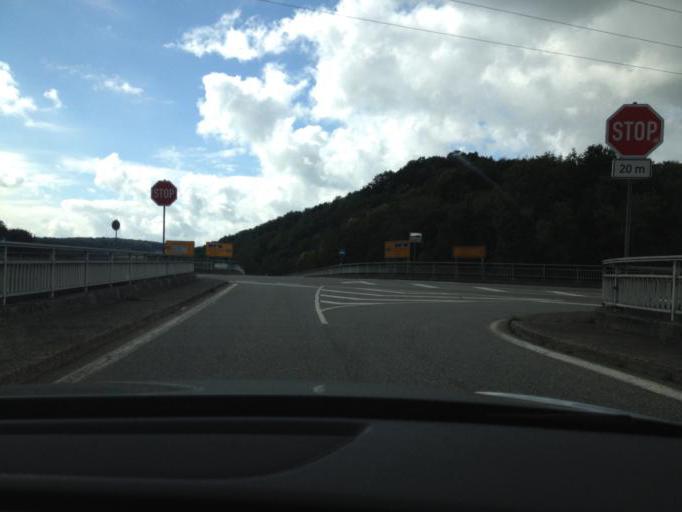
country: DE
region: Saarland
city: Sankt Wendel
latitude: 49.4488
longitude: 7.1482
